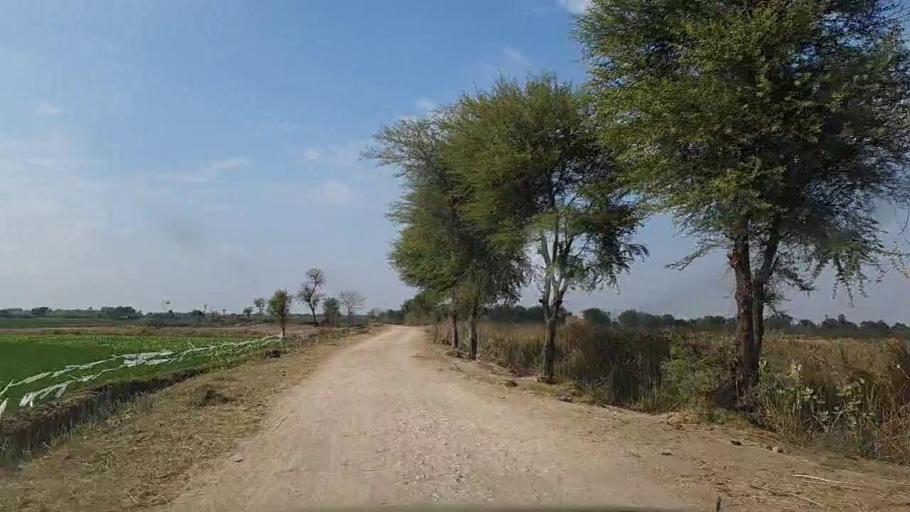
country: PK
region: Sindh
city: Sanghar
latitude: 26.2540
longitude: 69.0110
